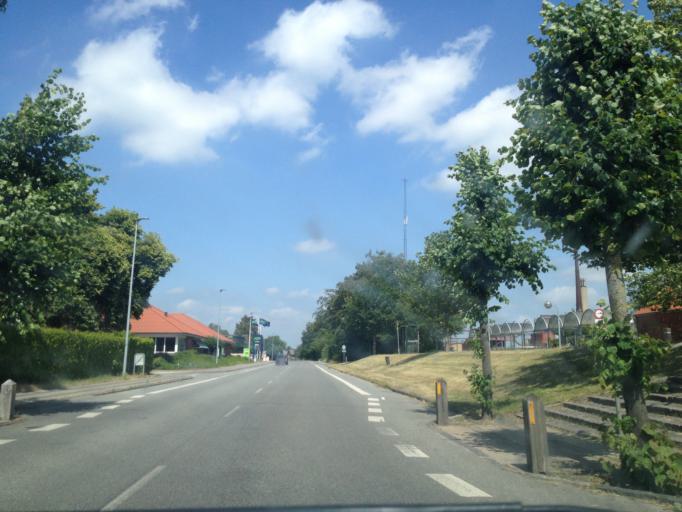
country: DK
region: South Denmark
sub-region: Kolding Kommune
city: Vamdrup
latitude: 55.4280
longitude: 9.2855
